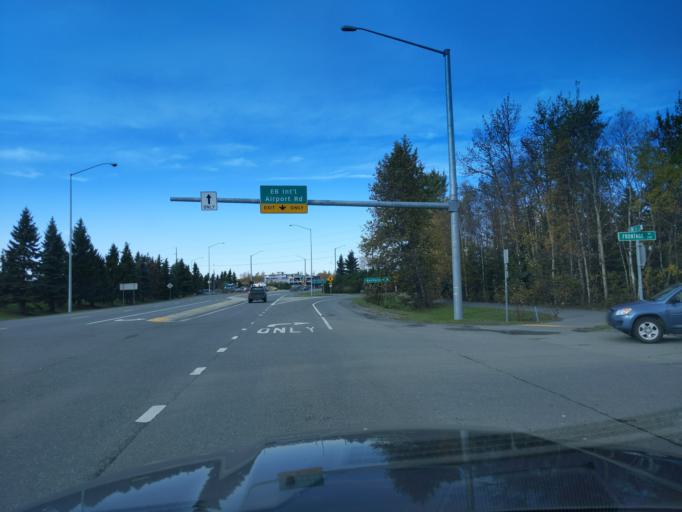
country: US
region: Alaska
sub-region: Anchorage Municipality
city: Anchorage
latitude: 61.1723
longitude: -149.9412
